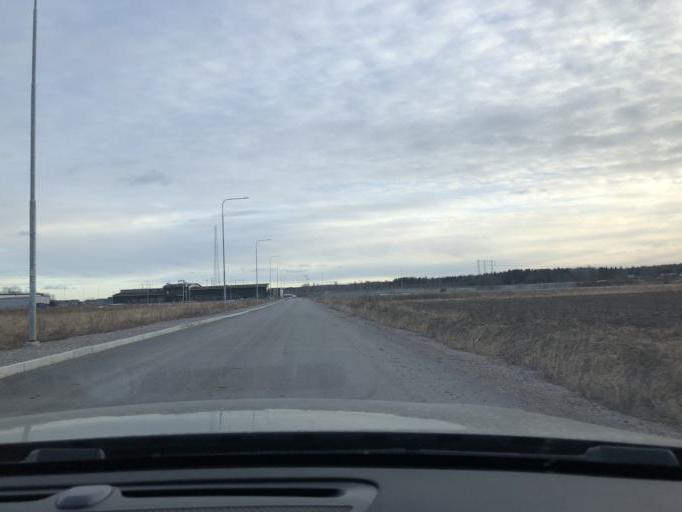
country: SE
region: Uppsala
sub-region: Tierps Kommun
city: Tierp
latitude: 60.3491
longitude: 17.4885
